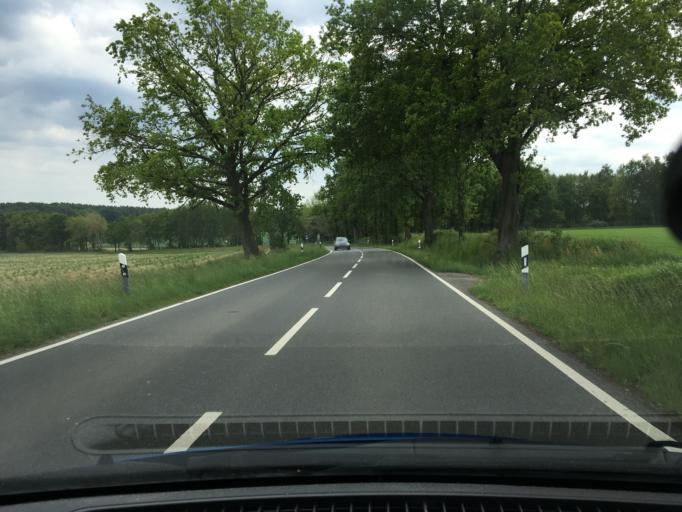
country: DE
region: Lower Saxony
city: Betzendorf
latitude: 53.1289
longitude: 10.3078
